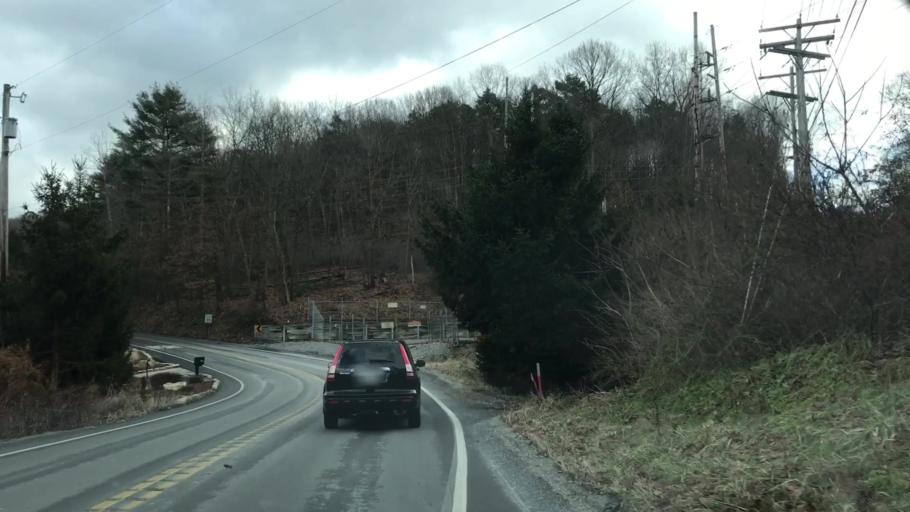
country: US
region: Pennsylvania
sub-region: Allegheny County
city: Franklin Park
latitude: 40.5921
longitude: -80.0746
